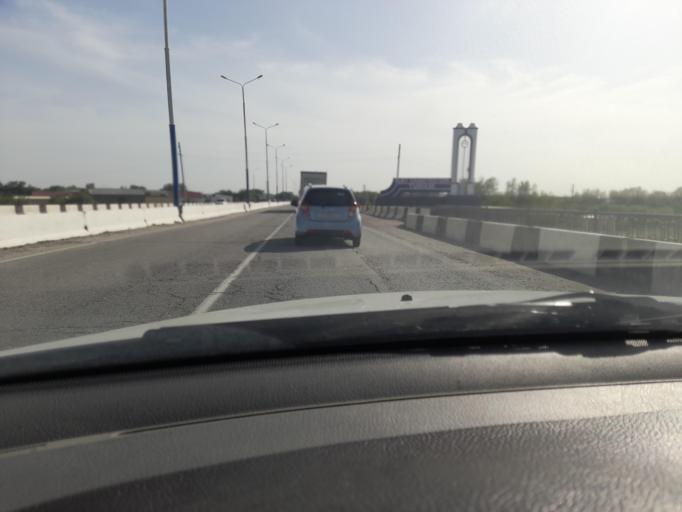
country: UZ
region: Samarqand
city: Kattaqo'rg'on
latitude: 39.9274
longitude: 66.3595
